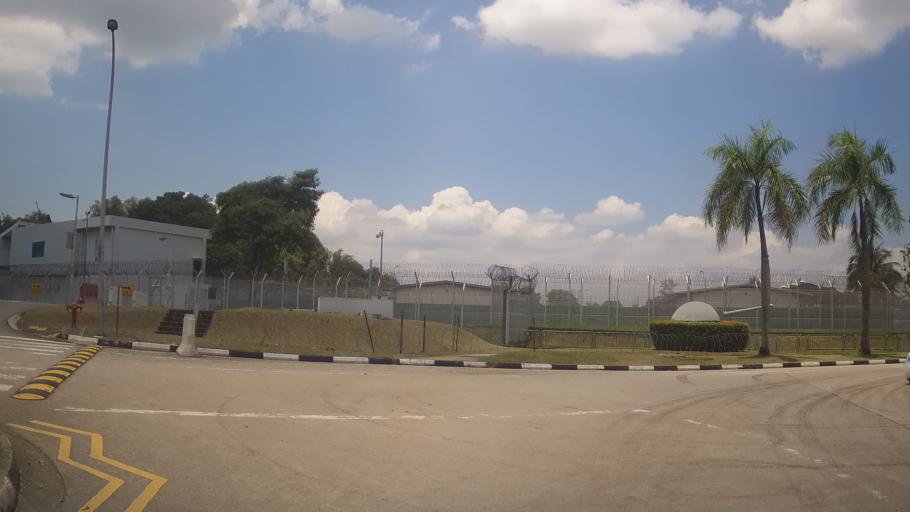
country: SG
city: Singapore
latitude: 1.2958
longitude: 103.6654
